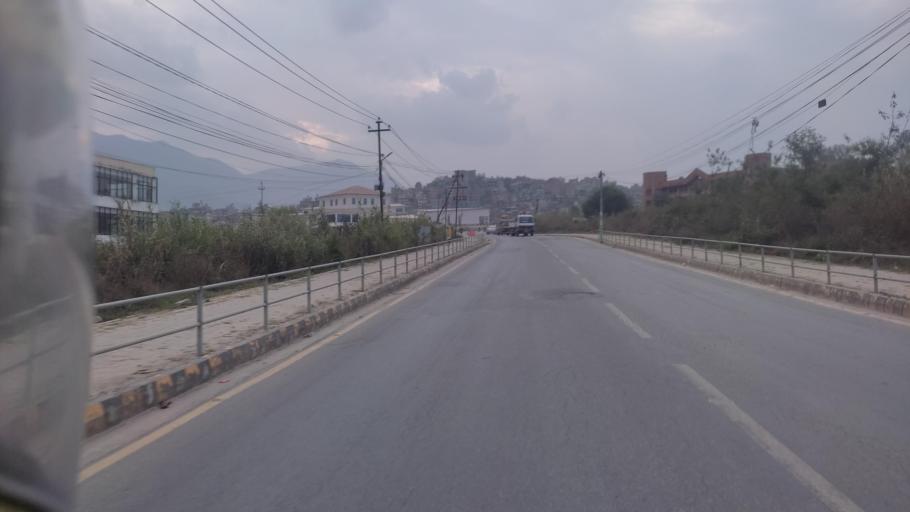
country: NP
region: Central Region
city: Kirtipur
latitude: 27.6758
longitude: 85.2870
